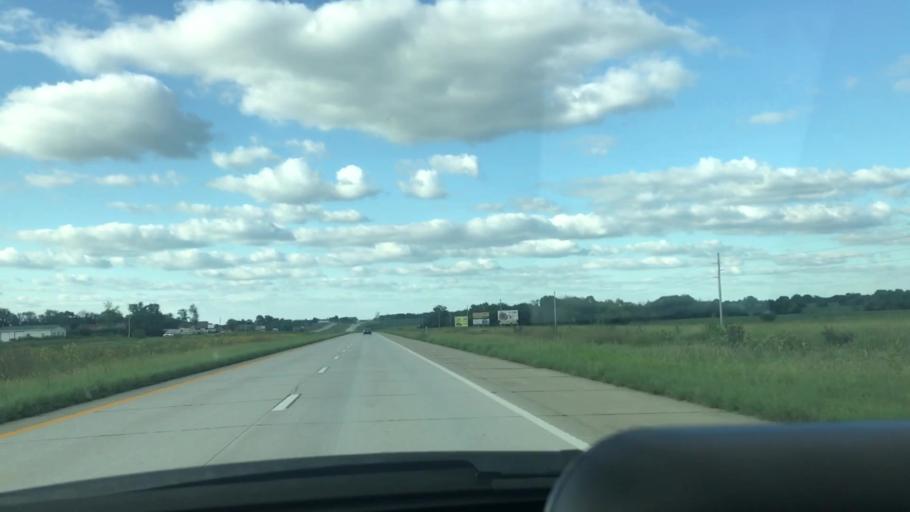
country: US
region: Missouri
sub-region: Benton County
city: Cole Camp
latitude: 38.5181
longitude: -93.2724
